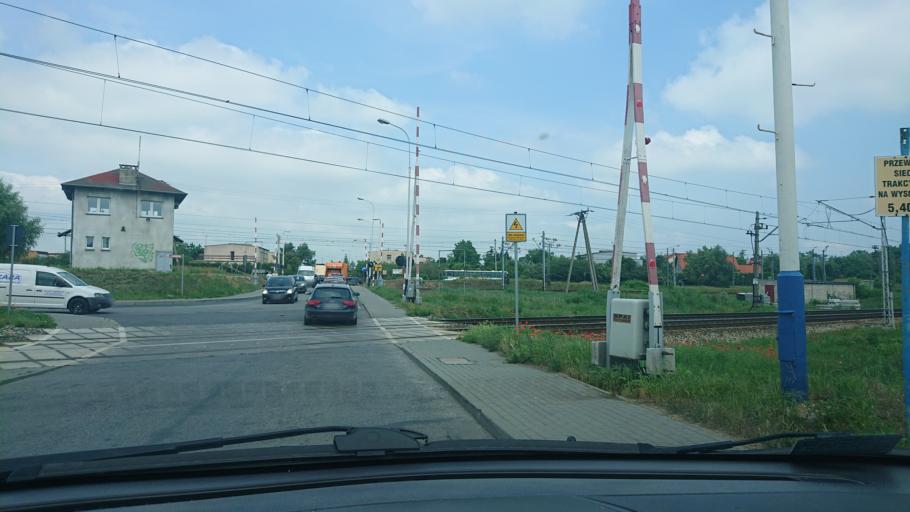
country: PL
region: Greater Poland Voivodeship
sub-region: Powiat gnieznienski
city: Gniezno
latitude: 52.5256
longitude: 17.5814
